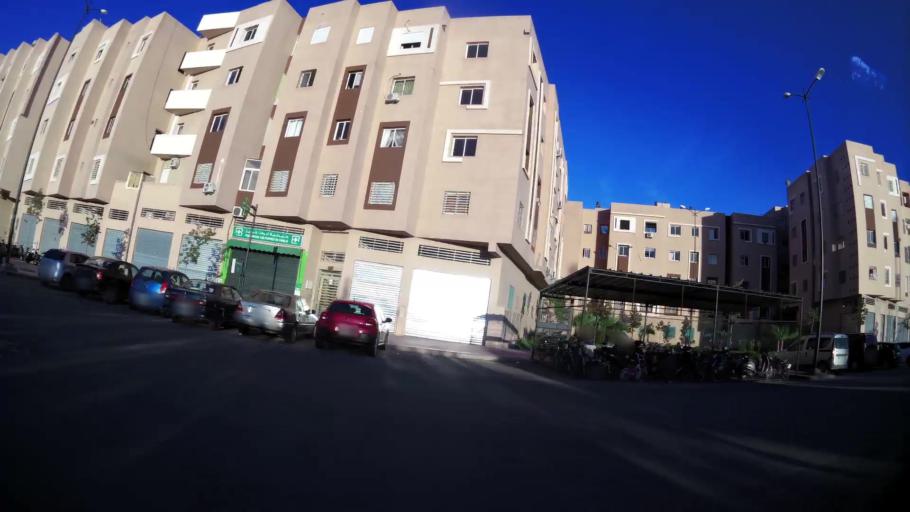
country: MA
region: Marrakech-Tensift-Al Haouz
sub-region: Marrakech
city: Marrakesh
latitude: 31.6492
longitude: -8.0389
